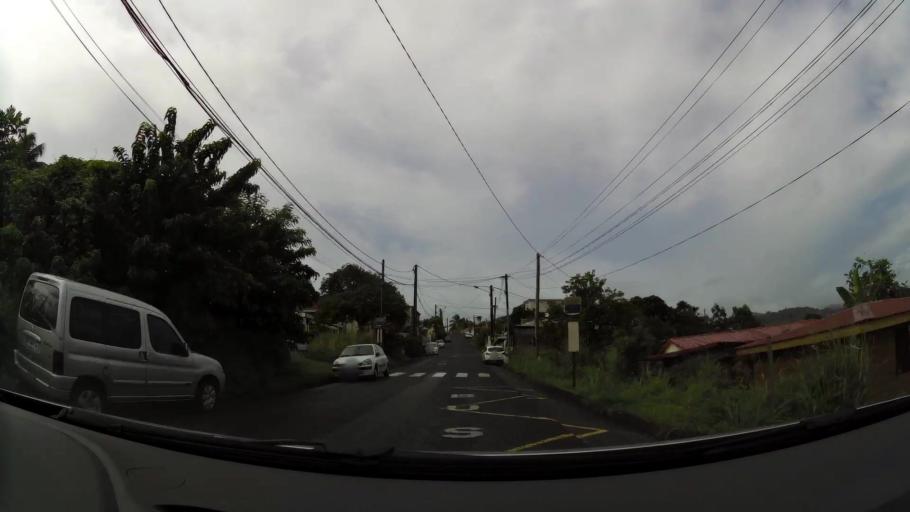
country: MQ
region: Martinique
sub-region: Martinique
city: Saint-Joseph
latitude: 14.6532
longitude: -61.0333
